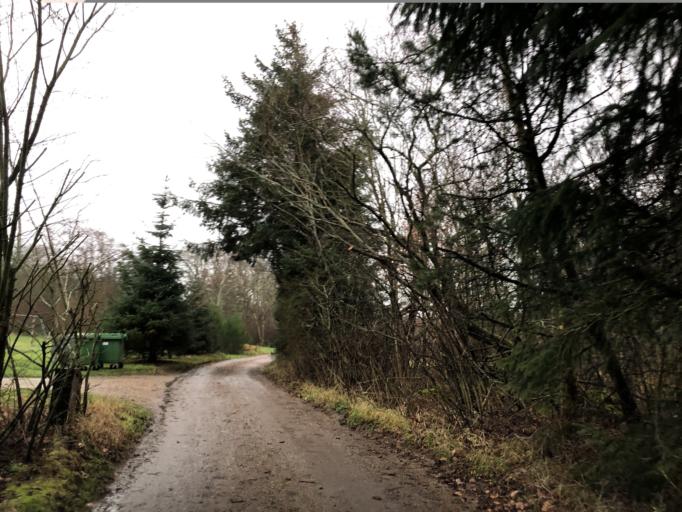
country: DK
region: Central Jutland
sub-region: Holstebro Kommune
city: Ulfborg
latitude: 56.2816
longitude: 8.1633
